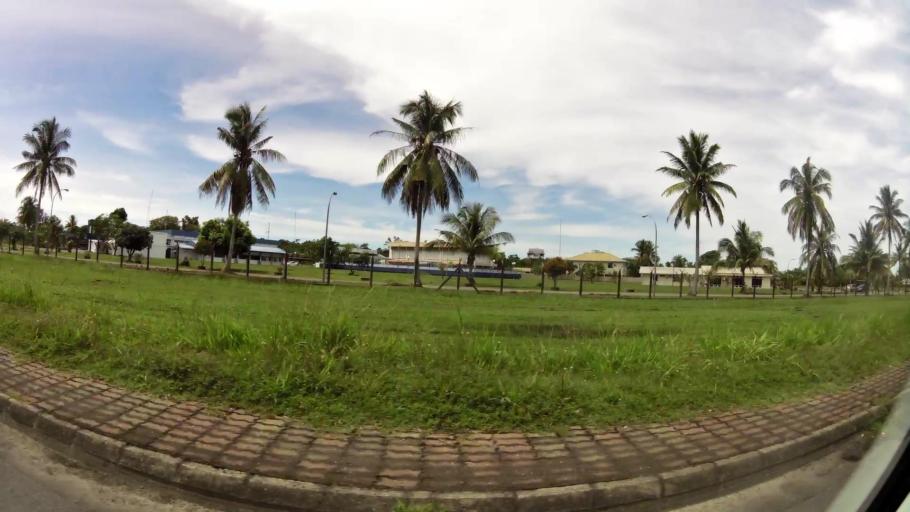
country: BN
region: Belait
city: Seria
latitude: 4.6002
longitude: 114.2846
